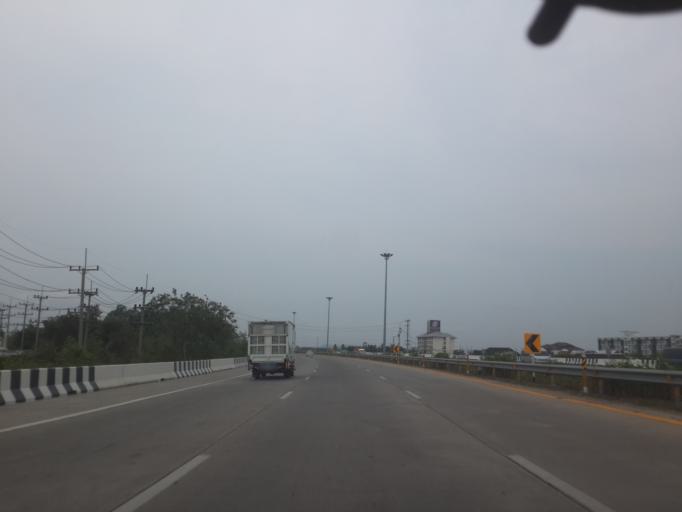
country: TH
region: Chon Buri
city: Phatthaya
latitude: 12.9434
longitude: 100.9173
